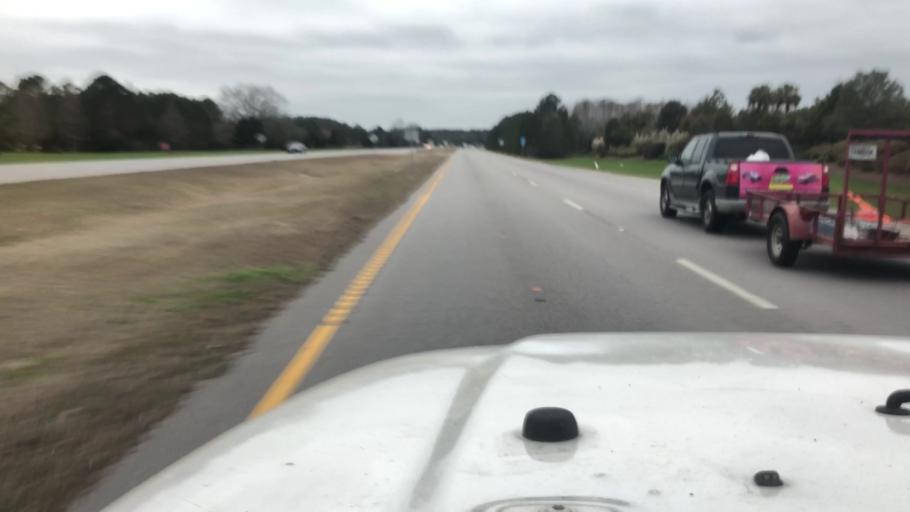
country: US
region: South Carolina
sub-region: Beaufort County
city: Bluffton
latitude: 32.3009
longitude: -80.9574
